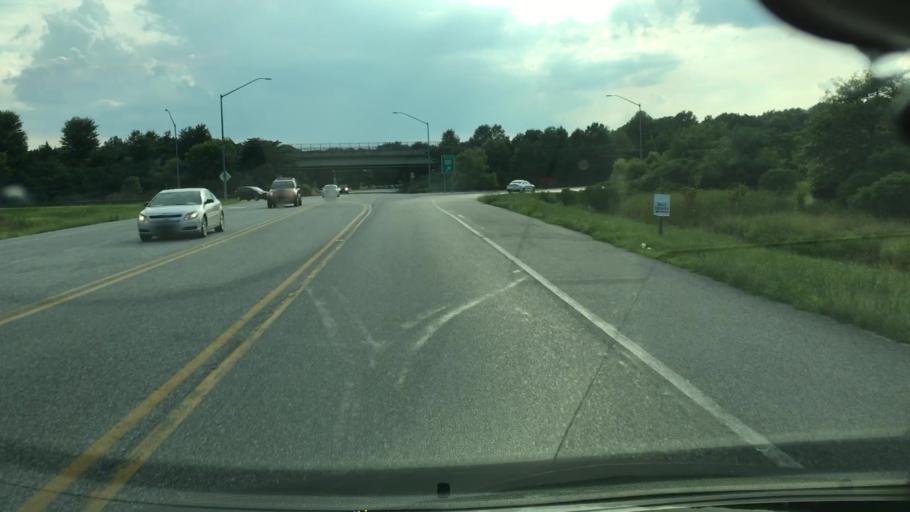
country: US
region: Maryland
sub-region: Worcester County
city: Ocean Pines
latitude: 38.3911
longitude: -75.2013
